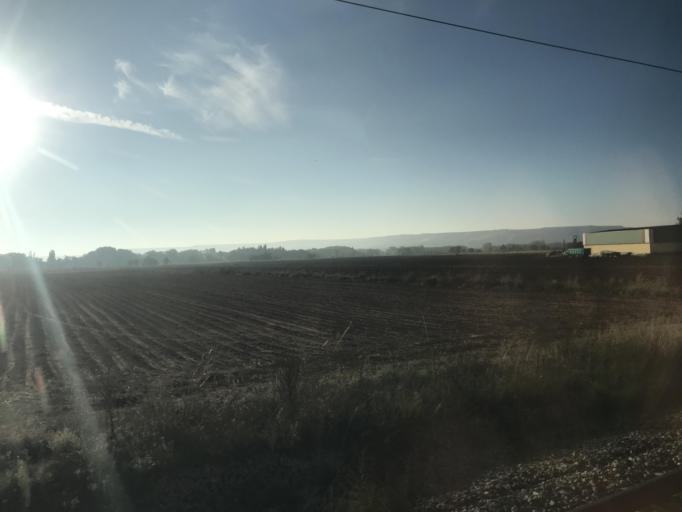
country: ES
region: Castille and Leon
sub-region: Provincia de Valladolid
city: Cubillas de Santa Marta
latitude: 41.8181
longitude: -4.5738
